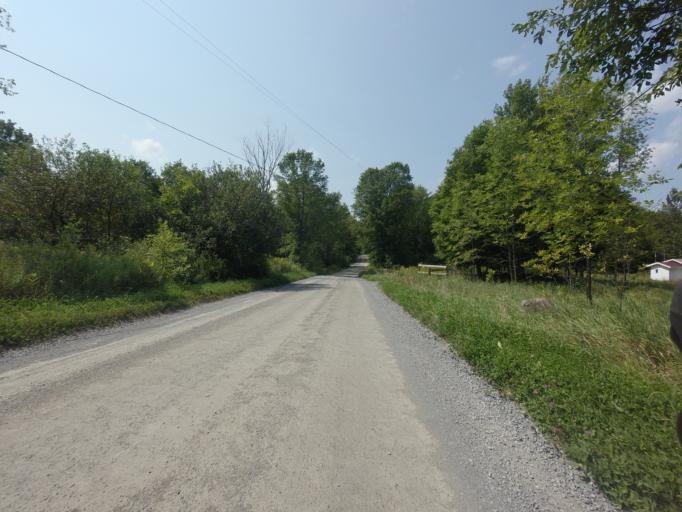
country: CA
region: Ontario
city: Kingston
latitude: 44.6431
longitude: -76.6430
